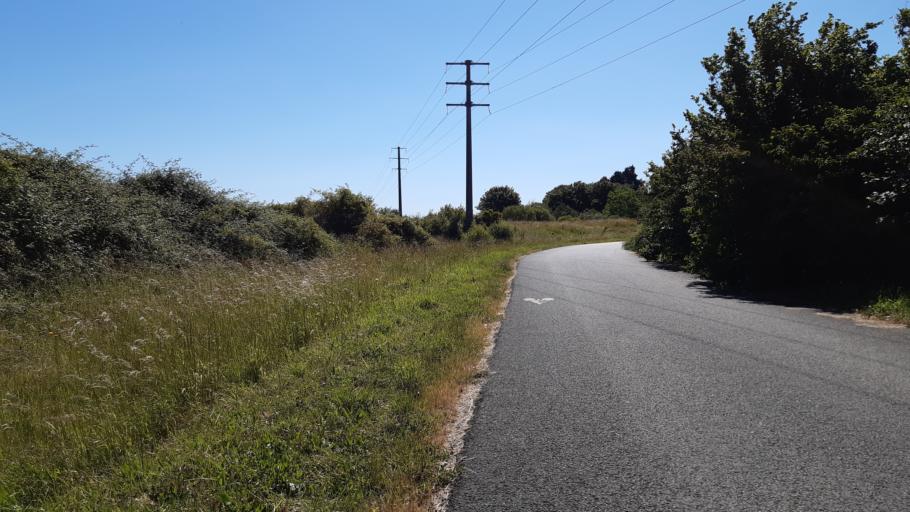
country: FR
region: Centre
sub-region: Departement d'Indre-et-Loire
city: Mettray
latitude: 47.4319
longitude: 0.6527
